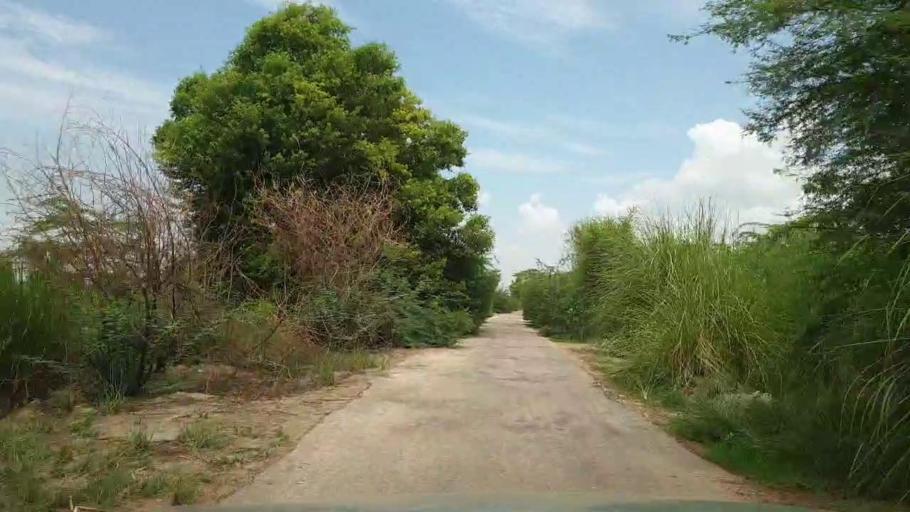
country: PK
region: Sindh
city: Bozdar
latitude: 27.0158
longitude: 68.9408
